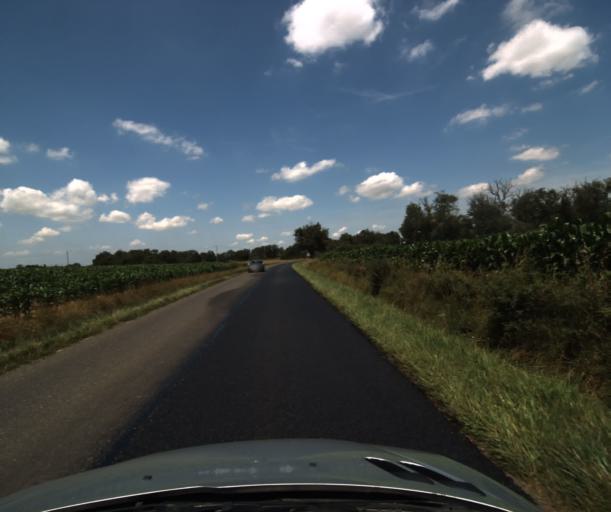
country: FR
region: Midi-Pyrenees
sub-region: Departement de la Haute-Garonne
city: Saint-Lys
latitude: 43.4938
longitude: 1.2025
